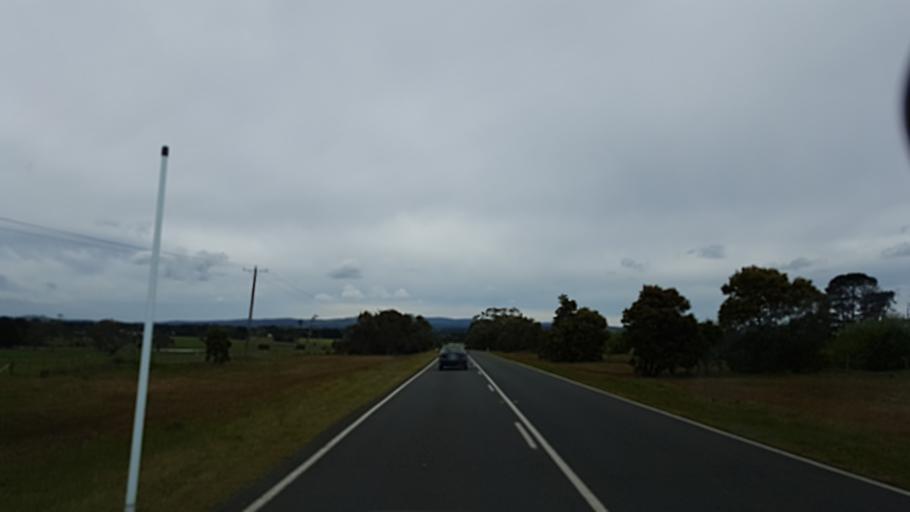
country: AU
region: Victoria
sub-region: Moorabool
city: Bacchus Marsh
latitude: -37.6149
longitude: 144.2128
